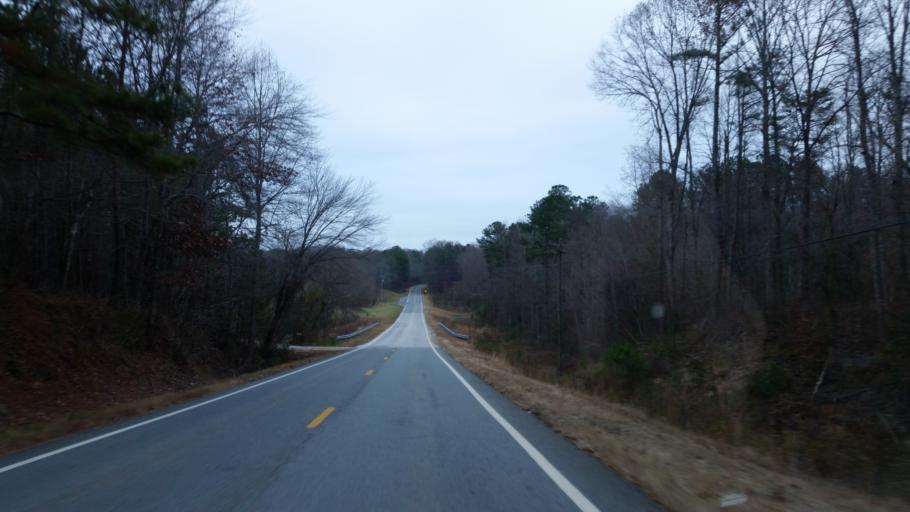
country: US
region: Georgia
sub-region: Dawson County
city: Dawsonville
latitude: 34.4463
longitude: -84.1117
